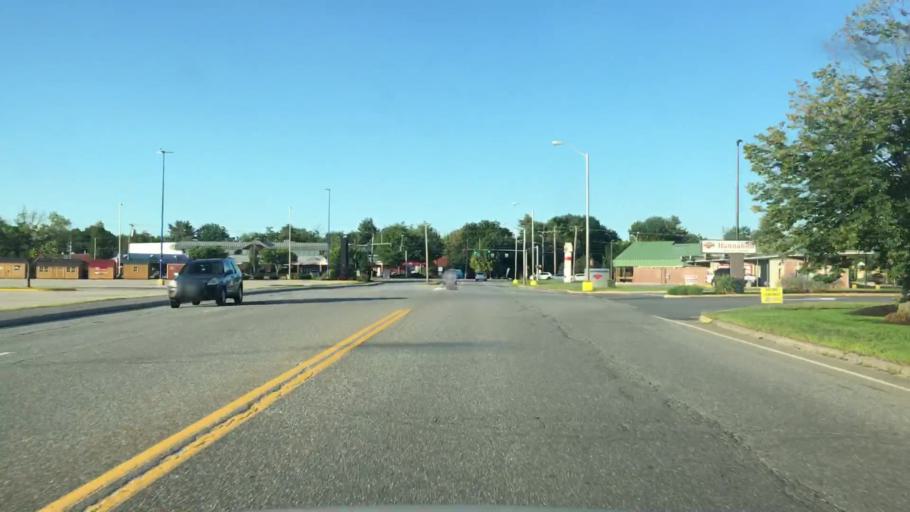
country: US
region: Maine
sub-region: Cumberland County
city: South Portland Gardens
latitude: 43.6346
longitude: -70.3309
